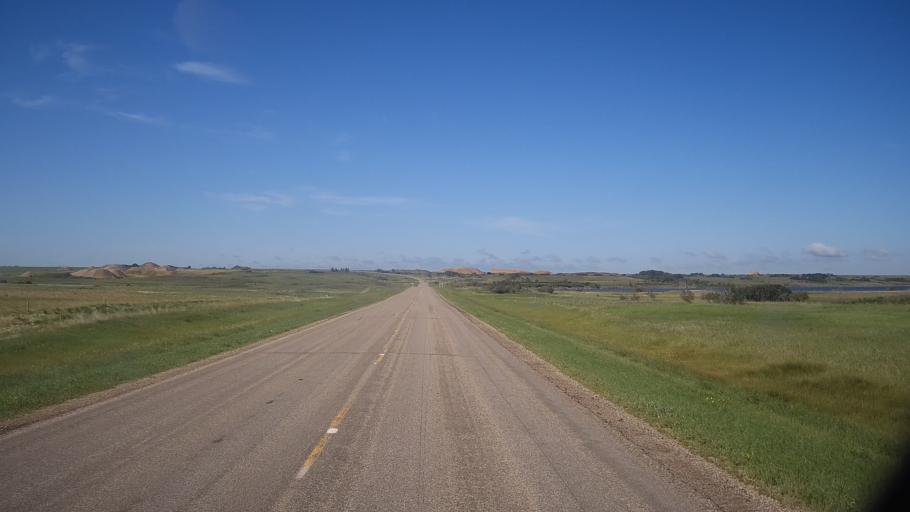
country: CA
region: Saskatchewan
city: Watrous
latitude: 51.7148
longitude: -105.3675
